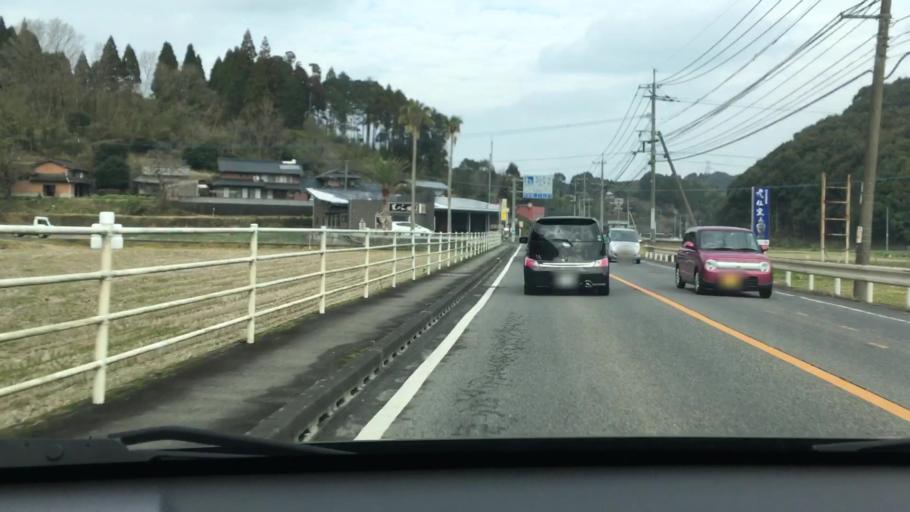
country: JP
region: Saga Prefecture
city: Imaricho-ko
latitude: 33.2985
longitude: 129.9174
